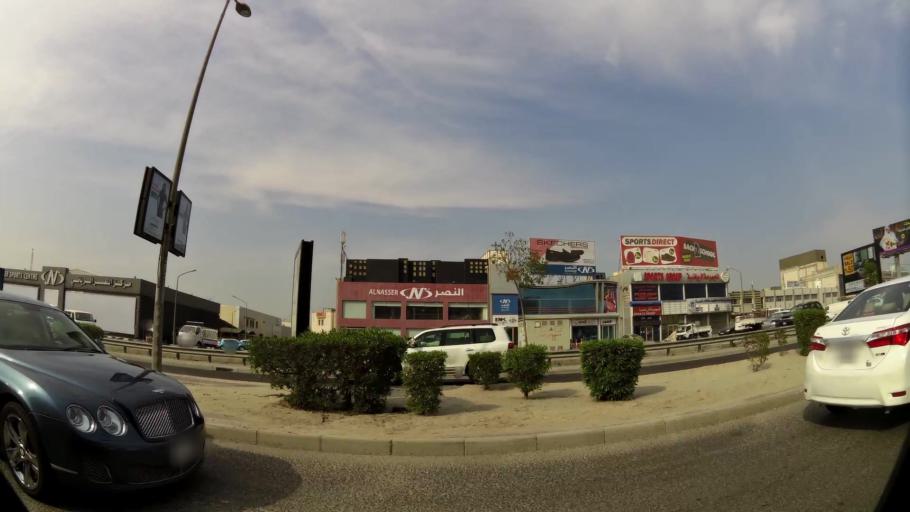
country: KW
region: Al Asimah
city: Ar Rabiyah
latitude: 29.3048
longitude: 47.9373
